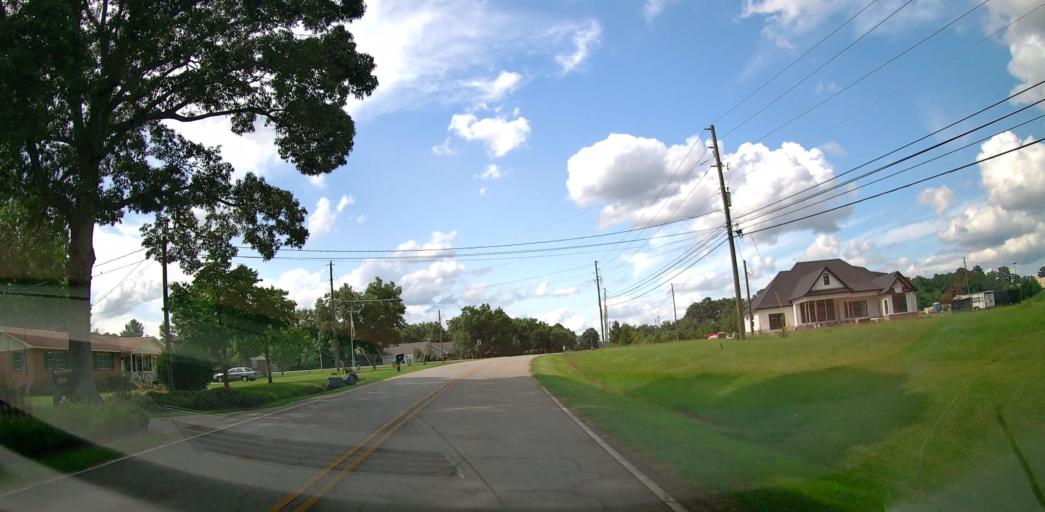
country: US
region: Georgia
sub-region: Houston County
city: Centerville
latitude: 32.5829
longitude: -83.6662
